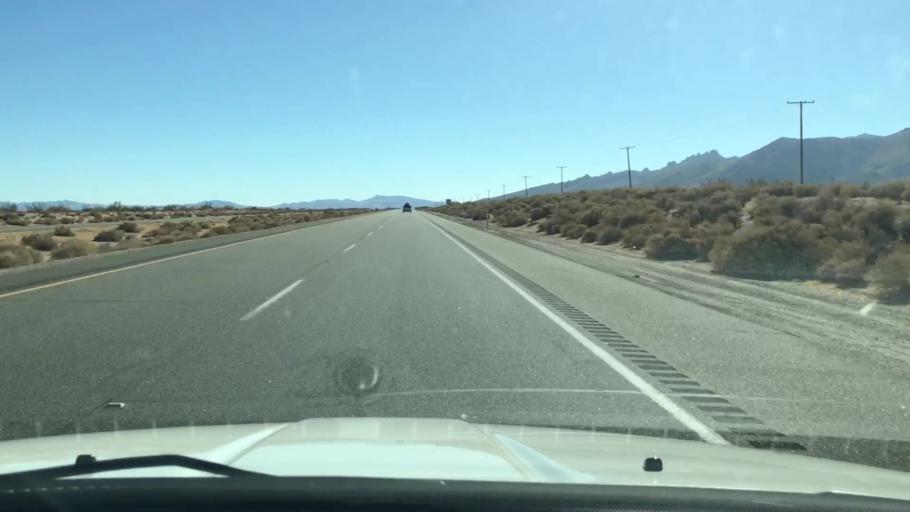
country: US
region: California
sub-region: Kern County
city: Inyokern
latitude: 35.7888
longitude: -117.8725
